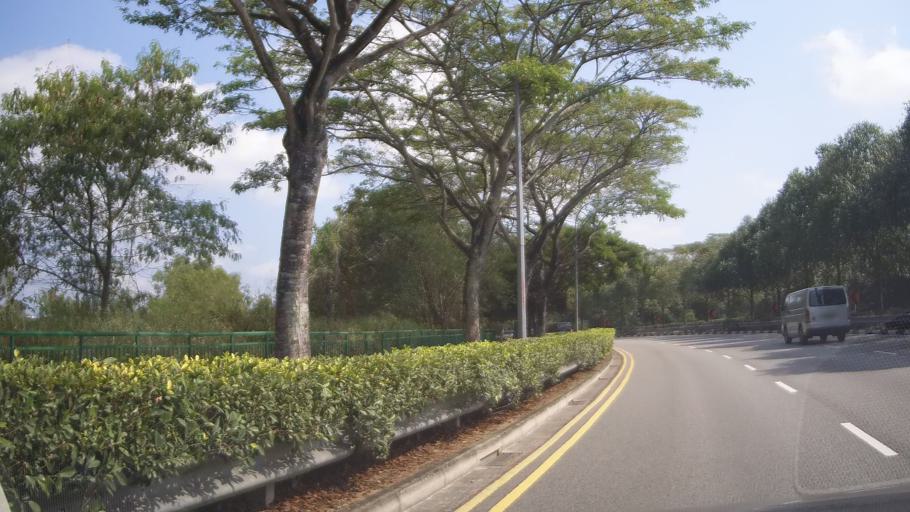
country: MY
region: Johor
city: Kampung Pasir Gudang Baru
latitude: 1.3754
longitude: 103.9093
